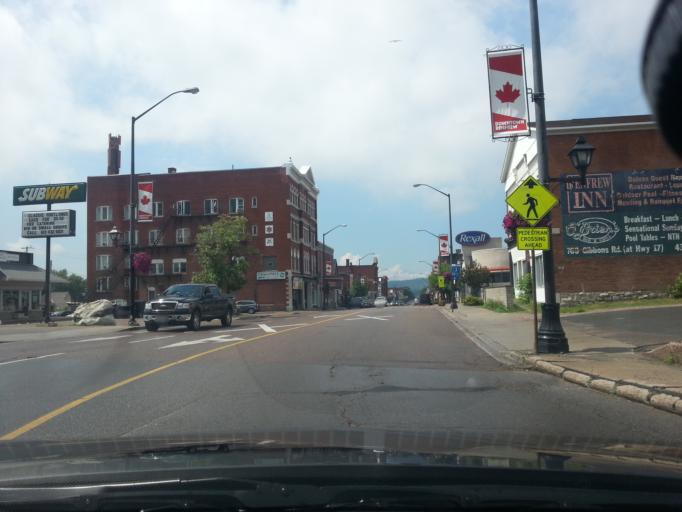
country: CA
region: Ontario
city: Renfrew
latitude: 45.4693
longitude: -76.6808
